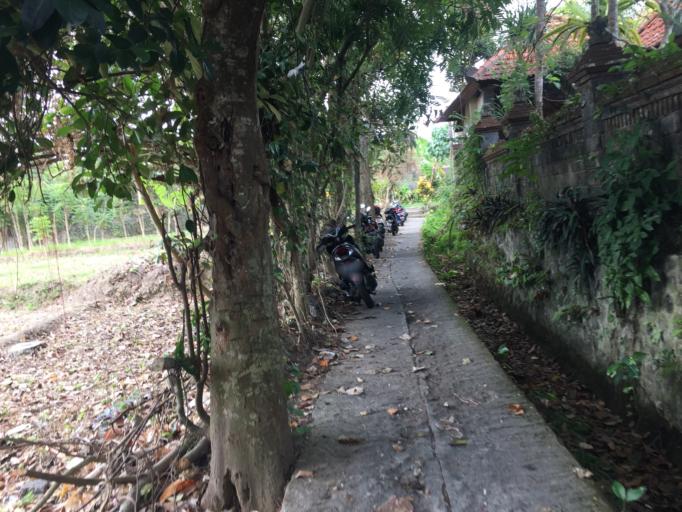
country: ID
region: Bali
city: Banjar Pande
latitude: -8.5060
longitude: 115.2518
